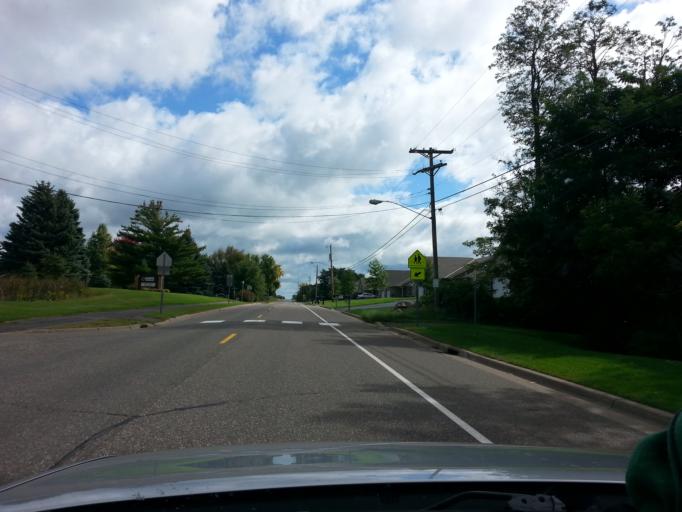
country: US
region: Minnesota
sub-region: Washington County
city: Oakdale
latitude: 44.9705
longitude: -92.9469
